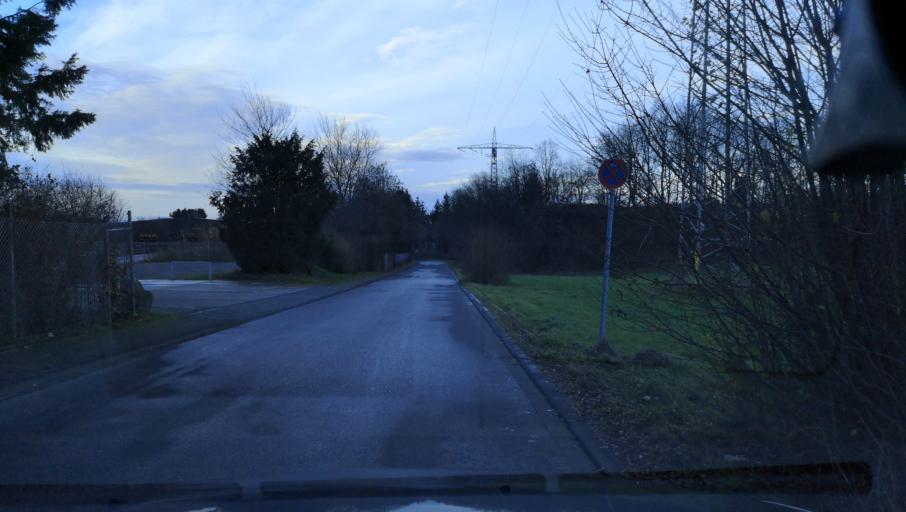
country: DE
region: North Rhine-Westphalia
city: Radevormwald
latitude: 51.1983
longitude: 7.3793
